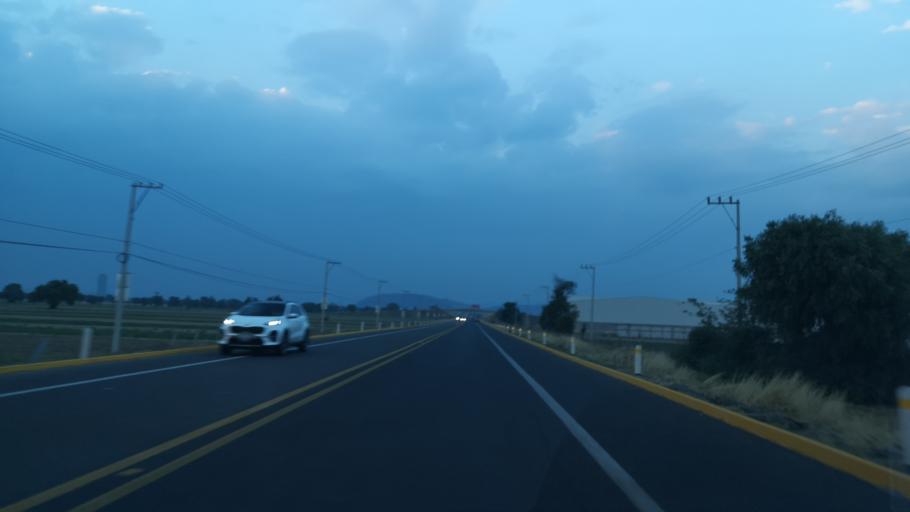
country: MX
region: Puebla
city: Santa Ana Xalmimilulco
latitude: 19.1884
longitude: -98.3687
